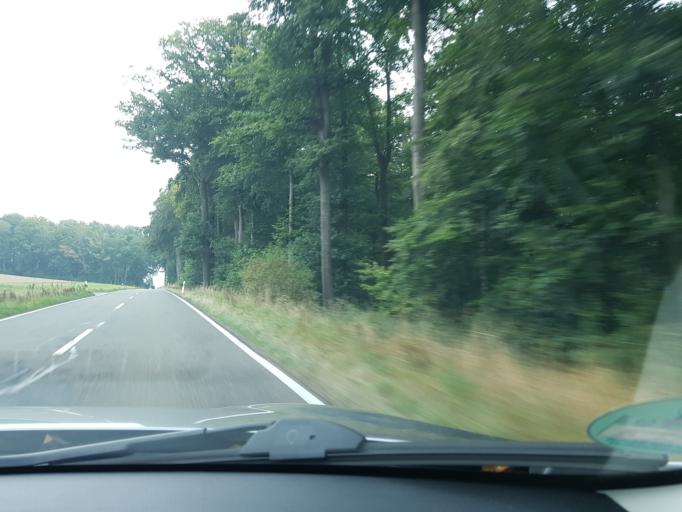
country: DE
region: Rheinland-Pfalz
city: Hainau
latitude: 50.2261
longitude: 7.7912
